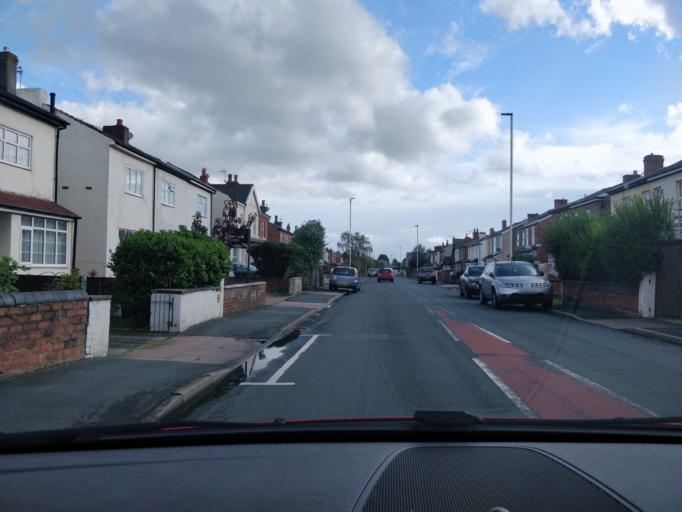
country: GB
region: England
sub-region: Sefton
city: Southport
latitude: 53.6292
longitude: -3.0073
